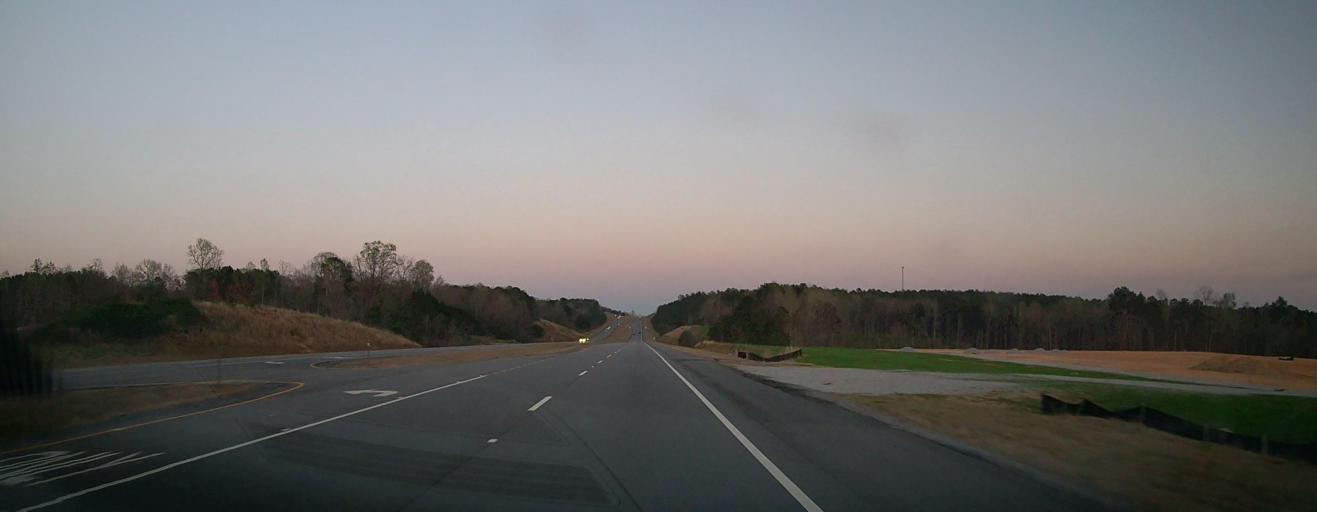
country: US
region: Alabama
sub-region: Tallapoosa County
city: Dadeville
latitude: 32.8800
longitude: -85.8381
